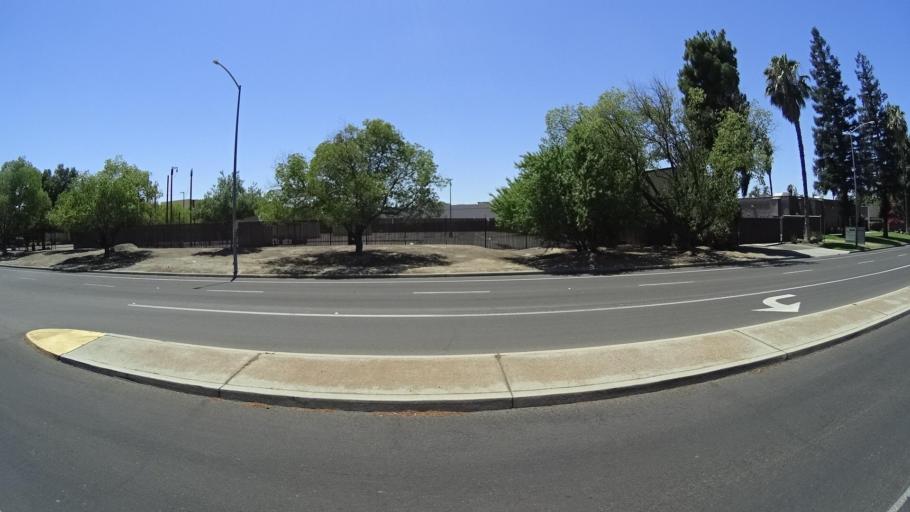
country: US
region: California
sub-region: Fresno County
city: Sunnyside
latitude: 36.7699
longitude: -119.7248
